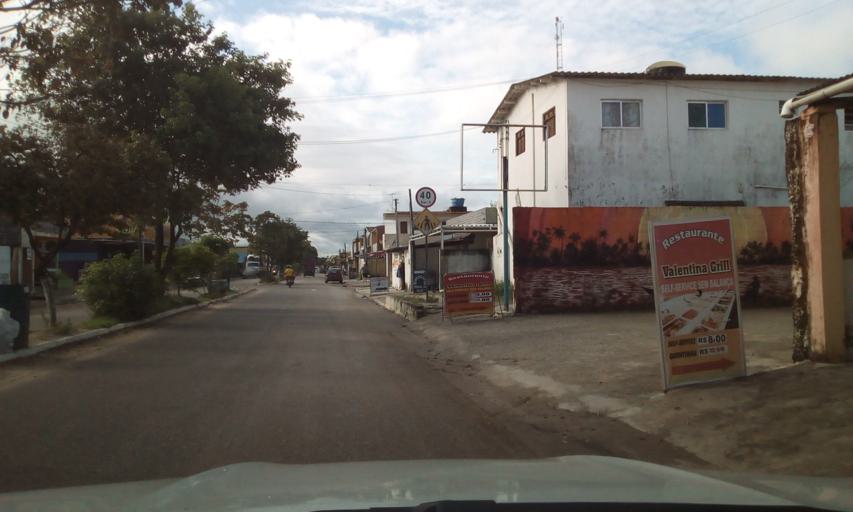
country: BR
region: Paraiba
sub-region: Conde
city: Conde
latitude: -7.2110
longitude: -34.8505
